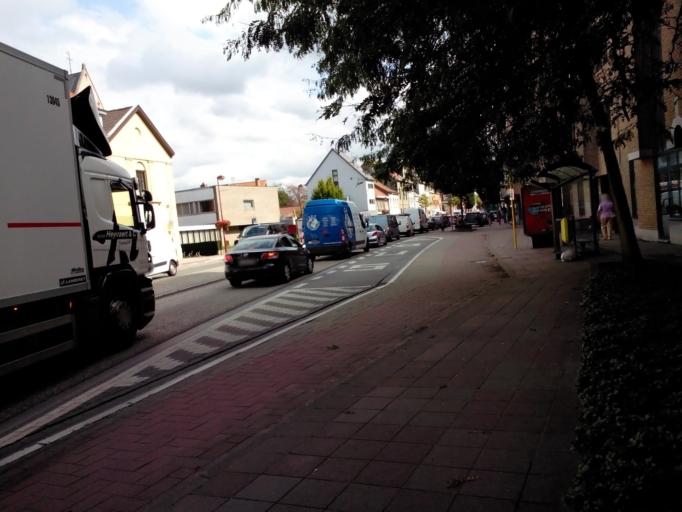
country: BE
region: Flanders
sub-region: Provincie Vlaams-Brabant
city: Asse
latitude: 50.9102
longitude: 4.2011
